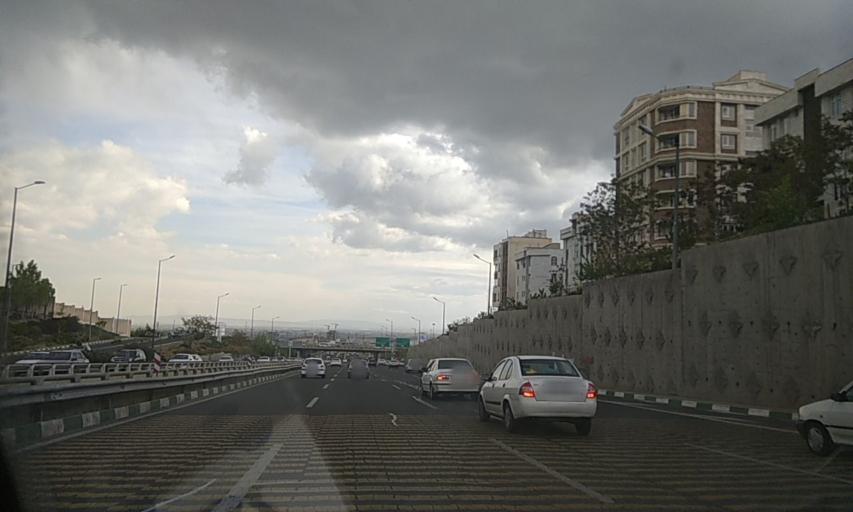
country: IR
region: Tehran
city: Tajrish
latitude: 35.7571
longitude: 51.2953
